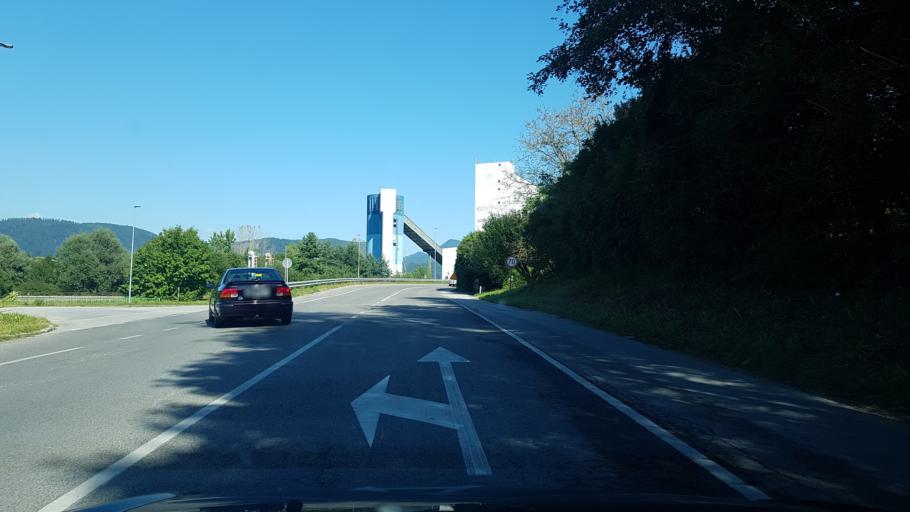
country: SI
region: Sostanj
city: Sostanj
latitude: 46.3686
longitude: 15.0726
